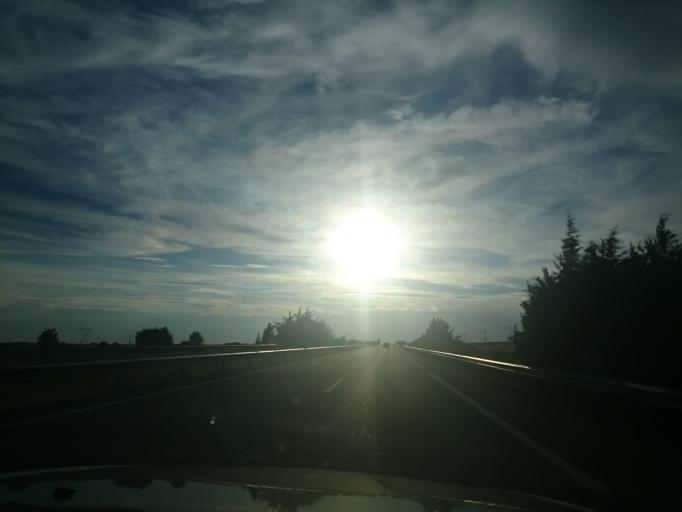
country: ES
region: Castille and Leon
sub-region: Provincia de Leon
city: Vallecillo
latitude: 42.4185
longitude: -5.2332
